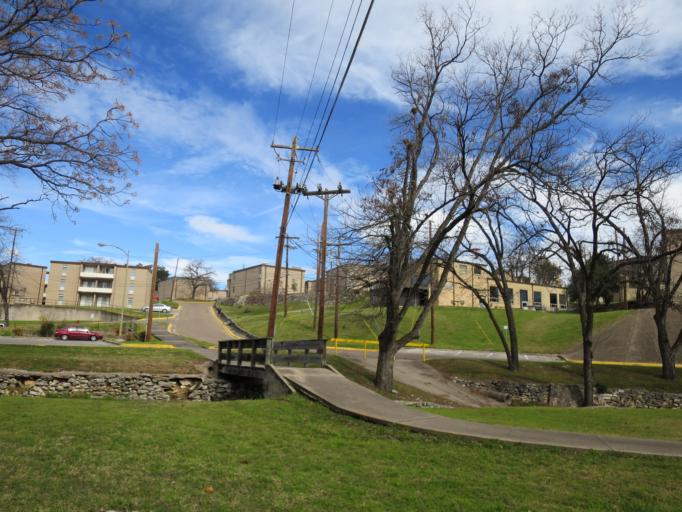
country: US
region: Texas
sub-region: Travis County
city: Austin
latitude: 30.2773
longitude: -97.7647
